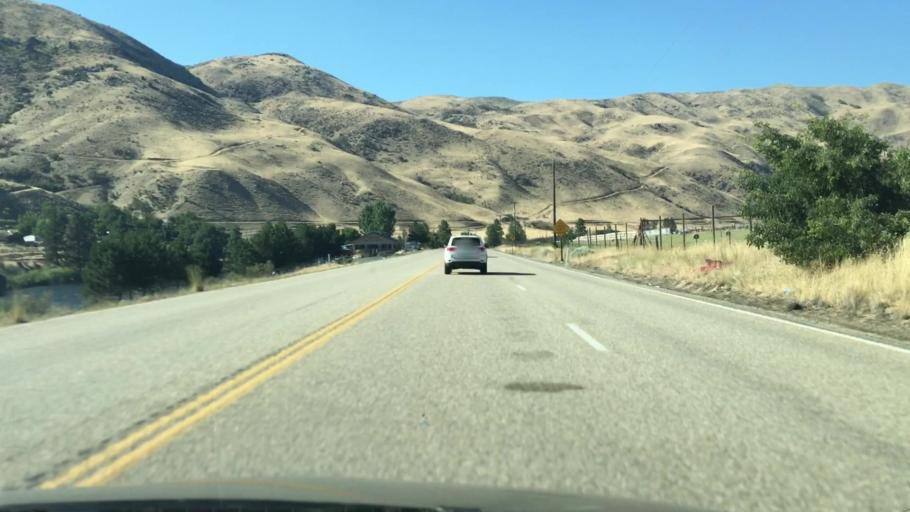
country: US
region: Idaho
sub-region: Gem County
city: Emmett
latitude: 43.9893
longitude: -116.1868
